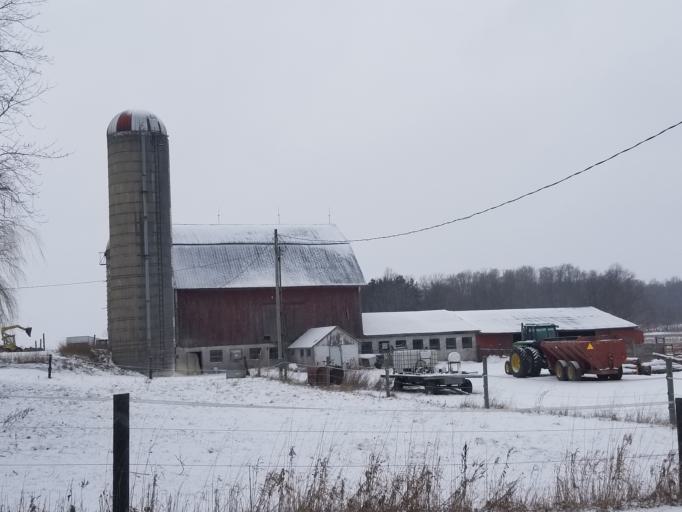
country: US
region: Michigan
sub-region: Wexford County
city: Cadillac
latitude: 44.1162
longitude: -85.2685
